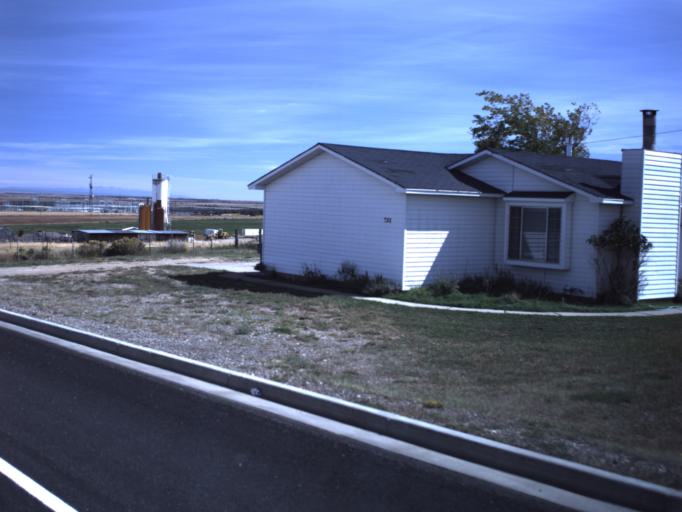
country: US
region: Utah
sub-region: San Juan County
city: Monticello
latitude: 37.8728
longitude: -109.3300
